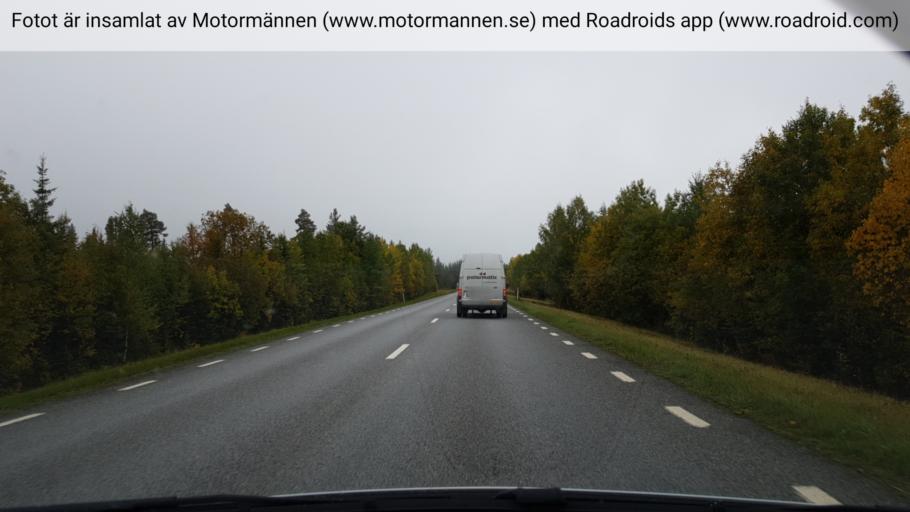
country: SE
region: Jaemtland
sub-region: Stroemsunds Kommun
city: Stroemsund
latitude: 63.5120
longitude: 15.2857
